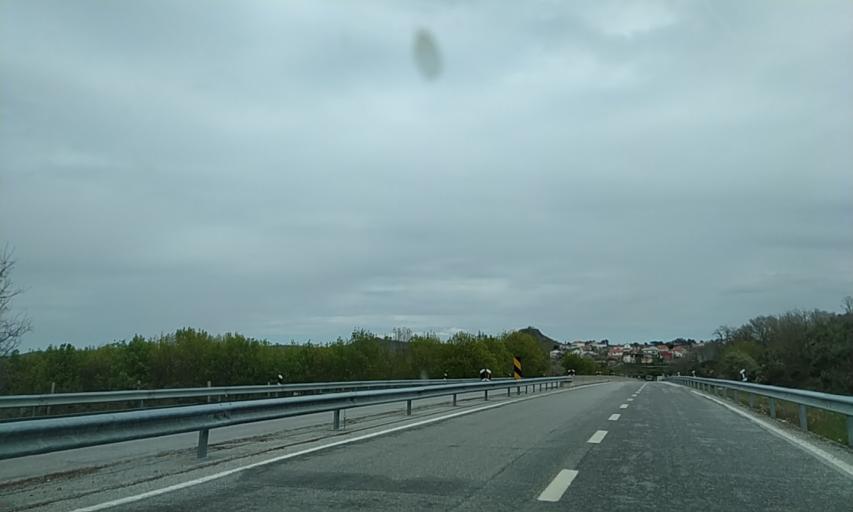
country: PT
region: Guarda
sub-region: Guarda
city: Guarda
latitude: 40.5865
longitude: -7.2704
